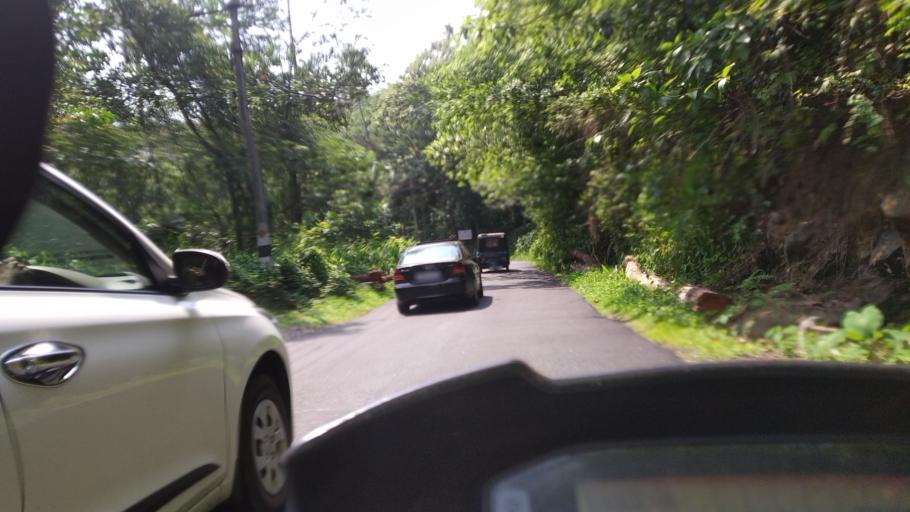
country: IN
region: Kerala
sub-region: Kottayam
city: Erattupetta
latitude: 9.6909
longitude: 76.8483
